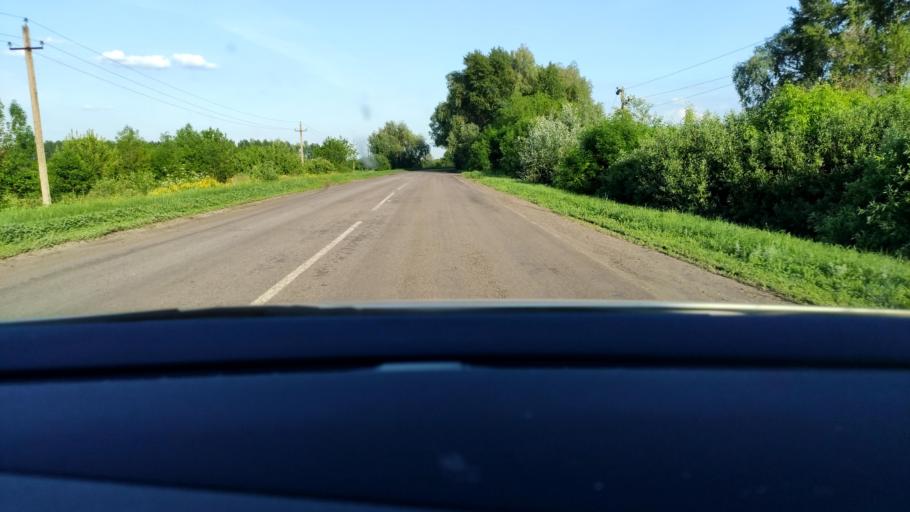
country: RU
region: Voronezj
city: Kashirskoye
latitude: 51.4911
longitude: 39.8479
